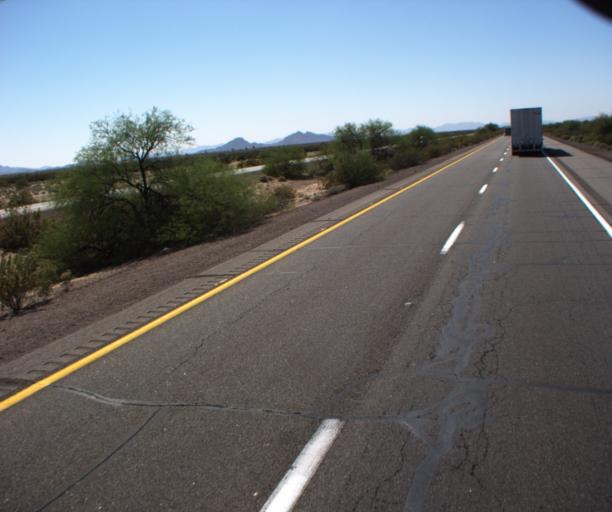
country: US
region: Arizona
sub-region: Yuma County
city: Wellton
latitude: 32.7064
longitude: -113.8701
